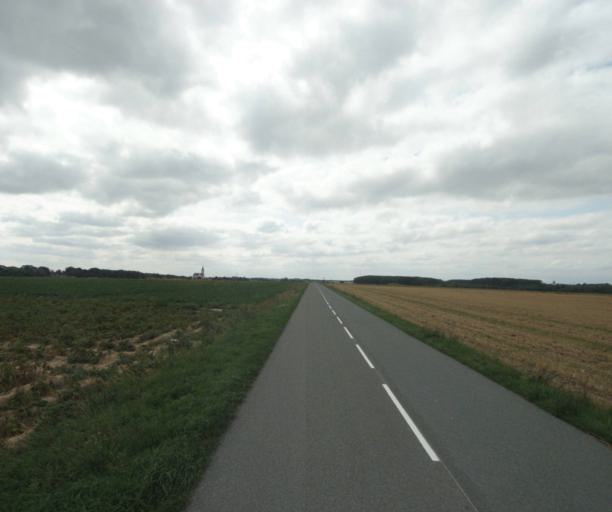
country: FR
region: Nord-Pas-de-Calais
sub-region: Departement du Nord
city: Gruson
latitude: 50.5866
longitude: 3.1994
